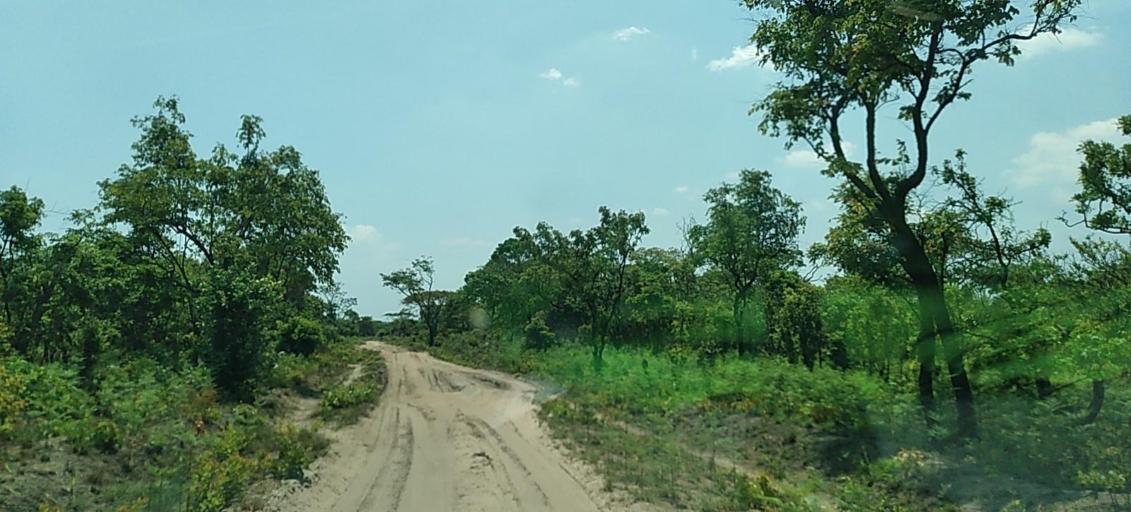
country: CD
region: Katanga
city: Kolwezi
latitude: -11.2980
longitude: 25.2256
